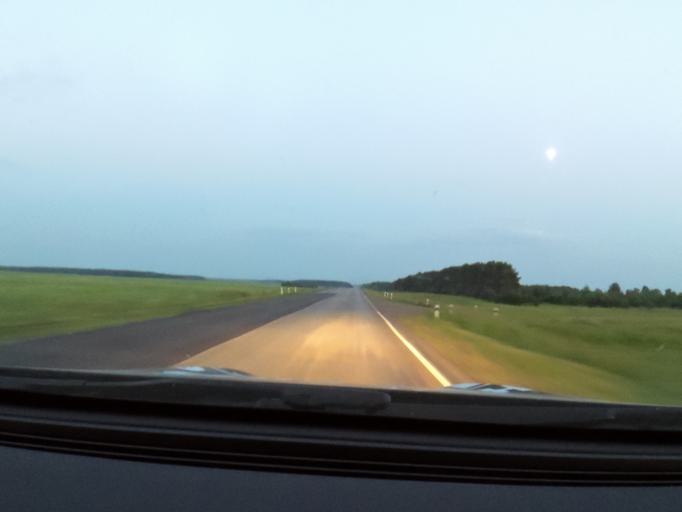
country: RU
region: Bashkortostan
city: Duvan
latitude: 56.1056
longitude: 58.0588
